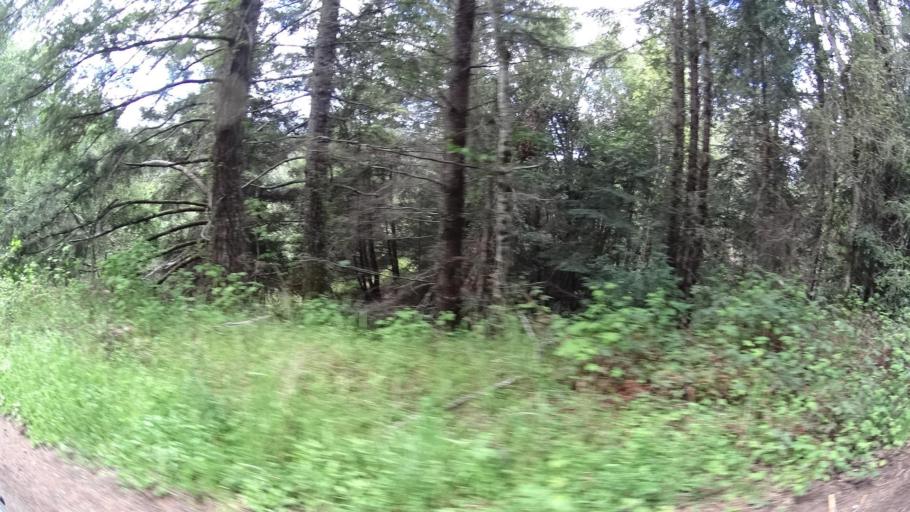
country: US
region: California
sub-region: Humboldt County
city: Blue Lake
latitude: 40.7895
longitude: -123.8814
